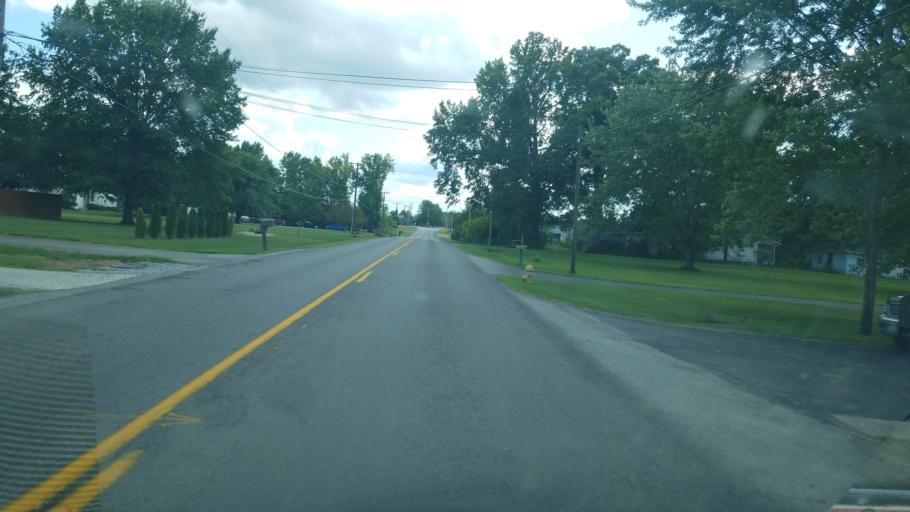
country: US
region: Ohio
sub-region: Allen County
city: Lima
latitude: 40.7603
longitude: -84.0706
